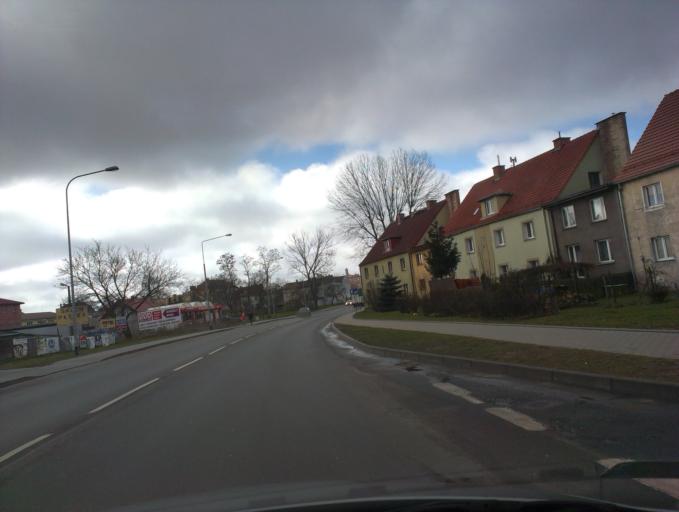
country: PL
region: West Pomeranian Voivodeship
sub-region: Powiat szczecinecki
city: Szczecinek
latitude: 53.6967
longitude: 16.7044
